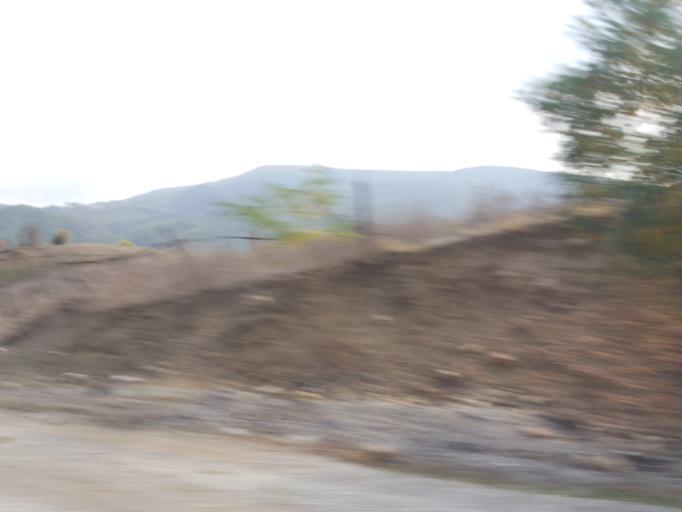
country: TR
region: Sinop
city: Sarayduzu
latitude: 41.3808
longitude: 34.9112
